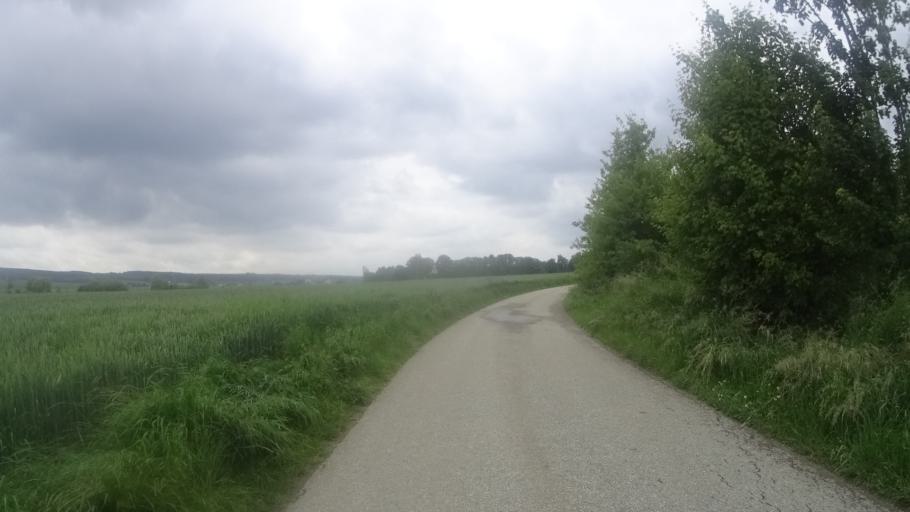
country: DE
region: Bavaria
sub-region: Lower Bavaria
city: Triftern
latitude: 48.4398
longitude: 13.0150
